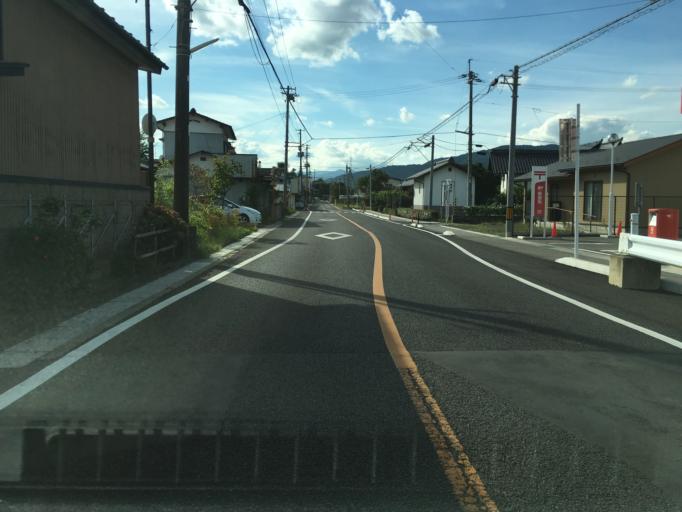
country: JP
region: Fukushima
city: Hobaramachi
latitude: 37.8258
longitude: 140.5254
